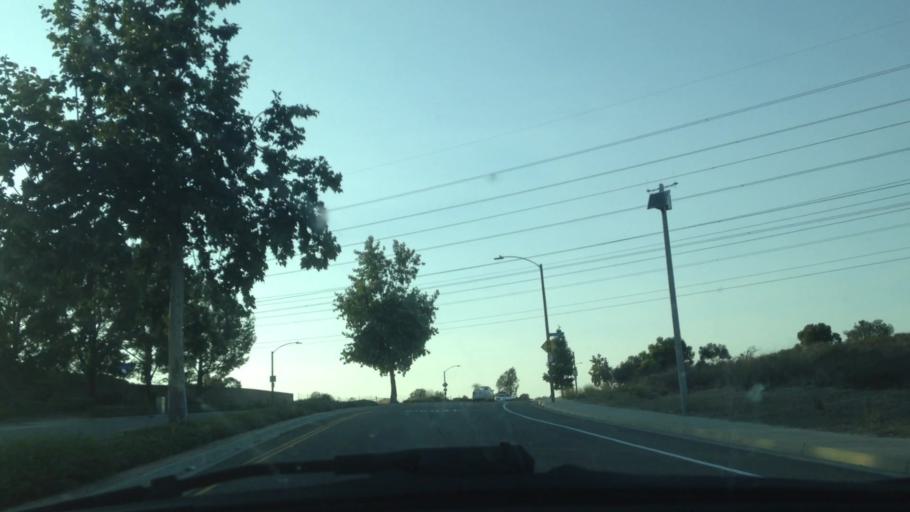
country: US
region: California
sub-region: Orange County
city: Villa Park
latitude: 33.8325
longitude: -117.7951
